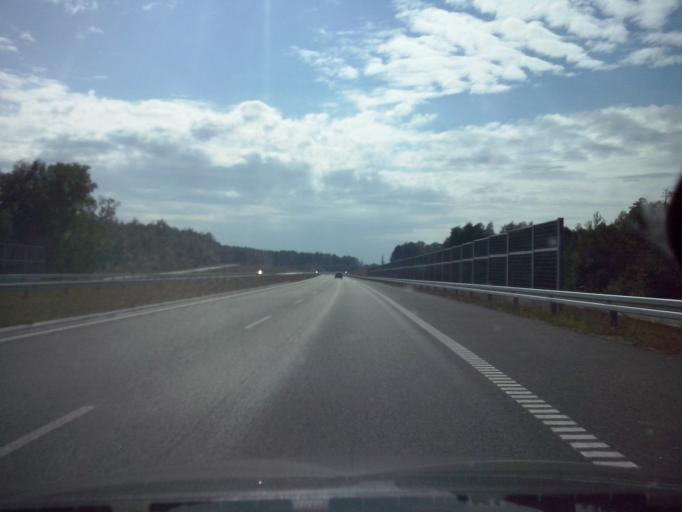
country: PL
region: Lesser Poland Voivodeship
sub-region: Powiat tarnowski
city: Jodlowka-Walki
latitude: 50.0918
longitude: 21.1582
